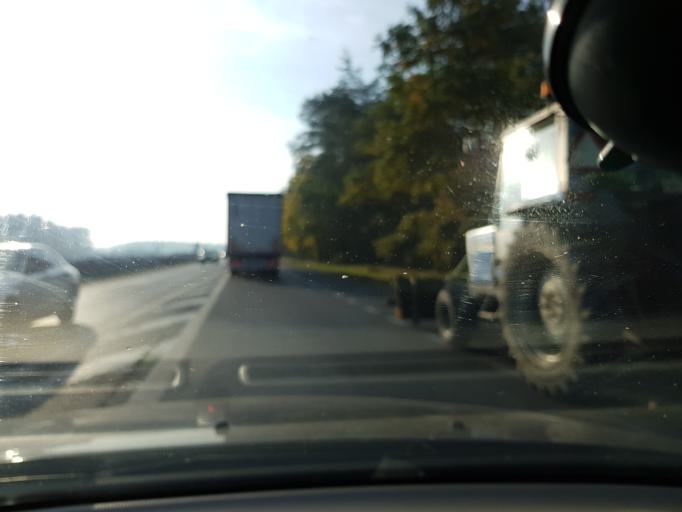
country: PL
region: Masovian Voivodeship
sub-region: Powiat otwocki
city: Otwock
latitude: 52.1541
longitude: 21.3125
